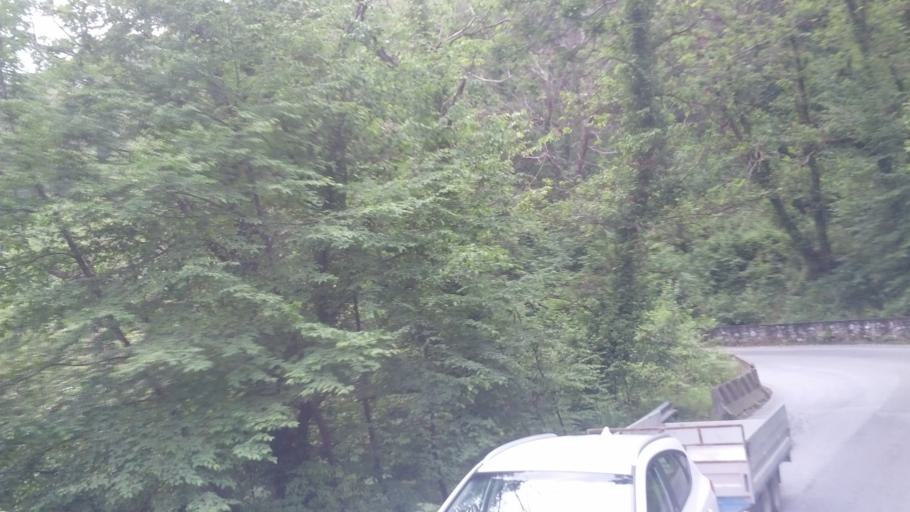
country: IT
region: Tuscany
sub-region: Provincia di Massa-Carrara
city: Massa
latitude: 44.0775
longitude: 10.1338
